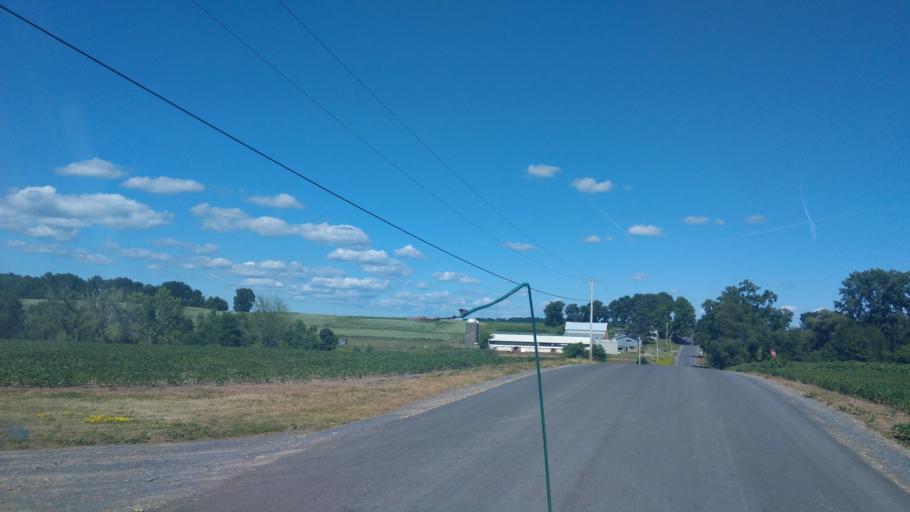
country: US
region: New York
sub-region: Wayne County
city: Clyde
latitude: 43.0257
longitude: -76.9051
